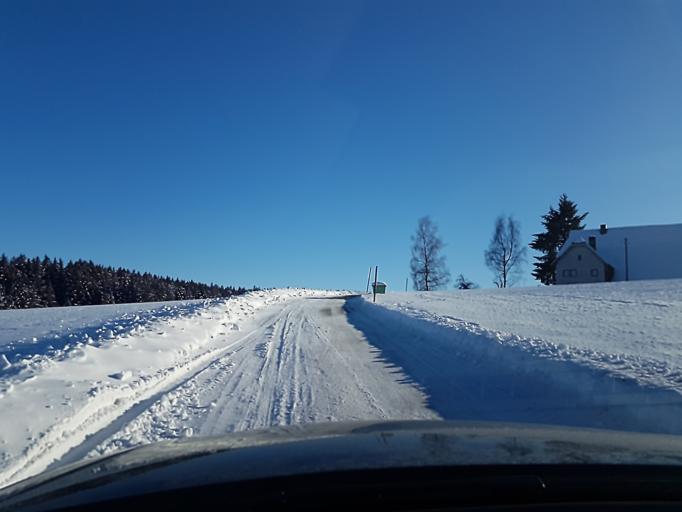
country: DE
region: Baden-Wuerttemberg
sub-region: Freiburg Region
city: Unterkirnach
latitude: 48.1069
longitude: 8.3602
